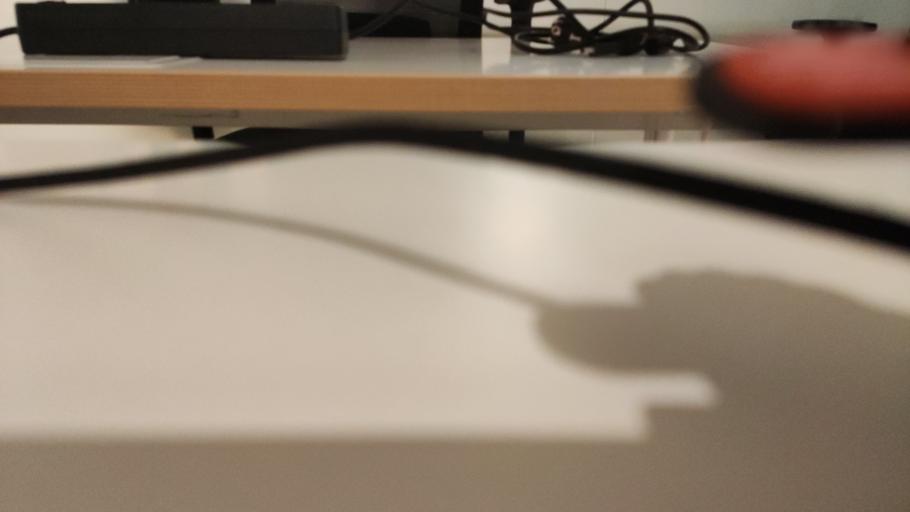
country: RU
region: Moskovskaya
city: Proletarskiy
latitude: 54.9769
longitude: 37.3544
